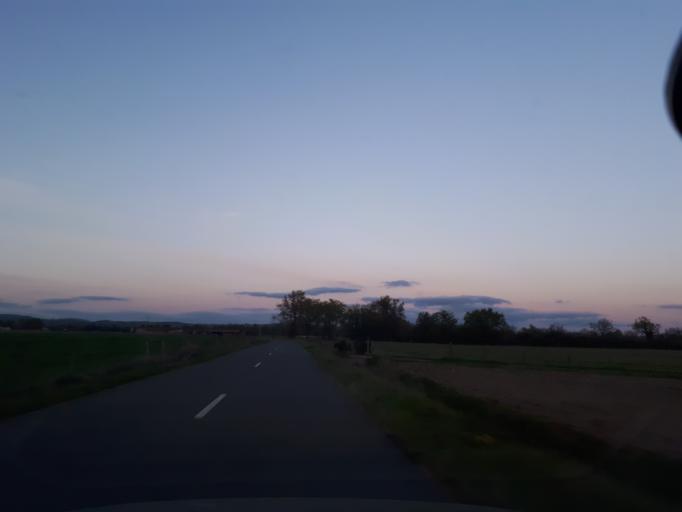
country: FR
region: Rhone-Alpes
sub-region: Departement de la Loire
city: Feurs
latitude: 45.7034
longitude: 4.2223
